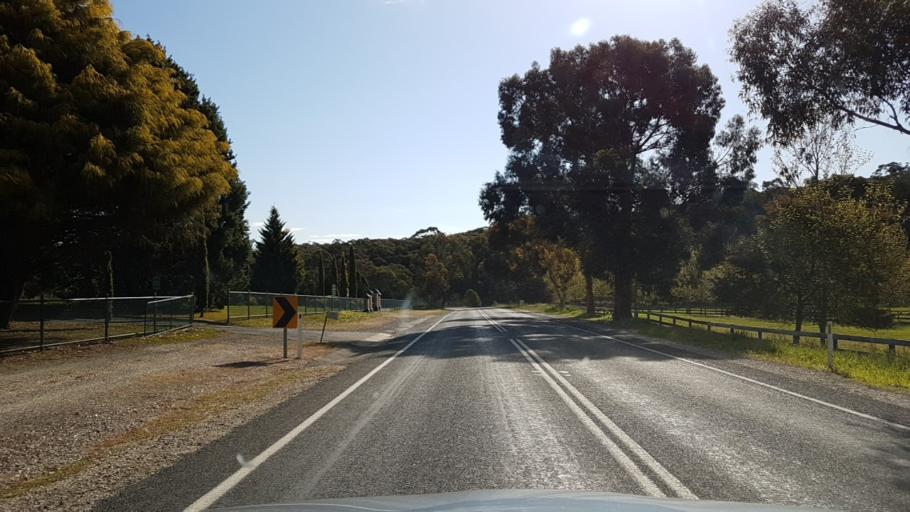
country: AU
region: South Australia
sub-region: Adelaide Hills
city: Lobethal
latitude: -34.8849
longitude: 138.8843
